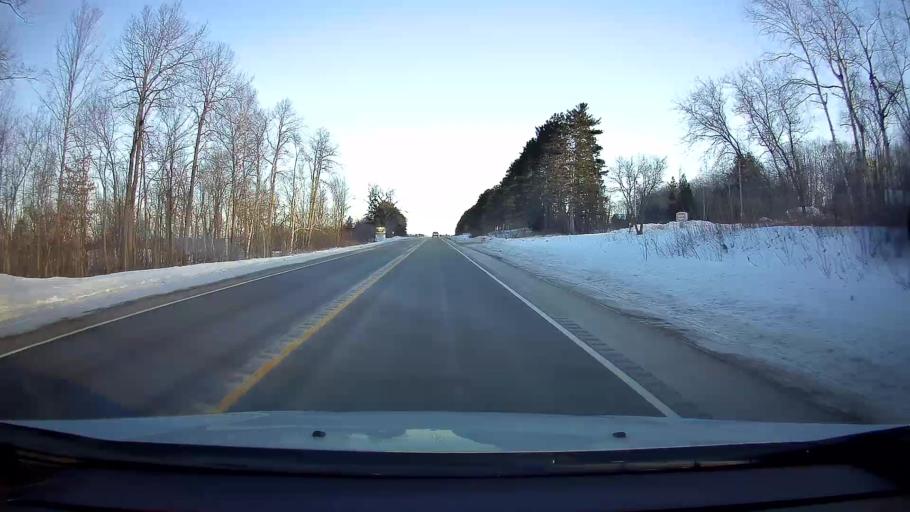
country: US
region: Wisconsin
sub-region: Washburn County
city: Shell Lake
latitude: 45.7596
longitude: -91.9140
